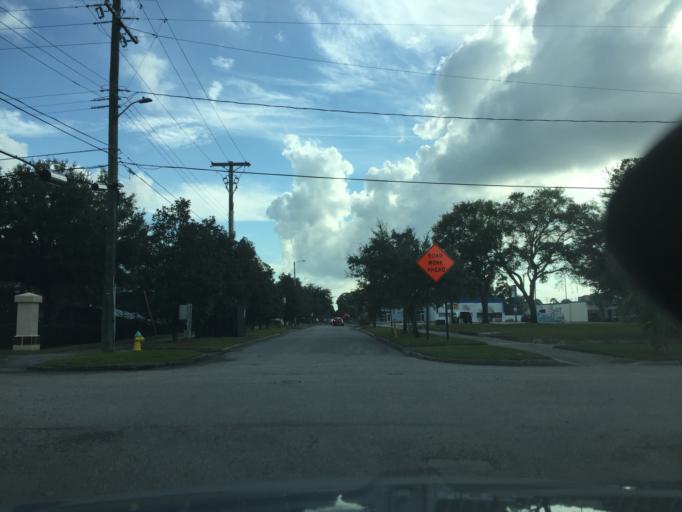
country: US
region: Florida
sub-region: Hillsborough County
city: Tampa
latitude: 27.9459
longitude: -82.4789
